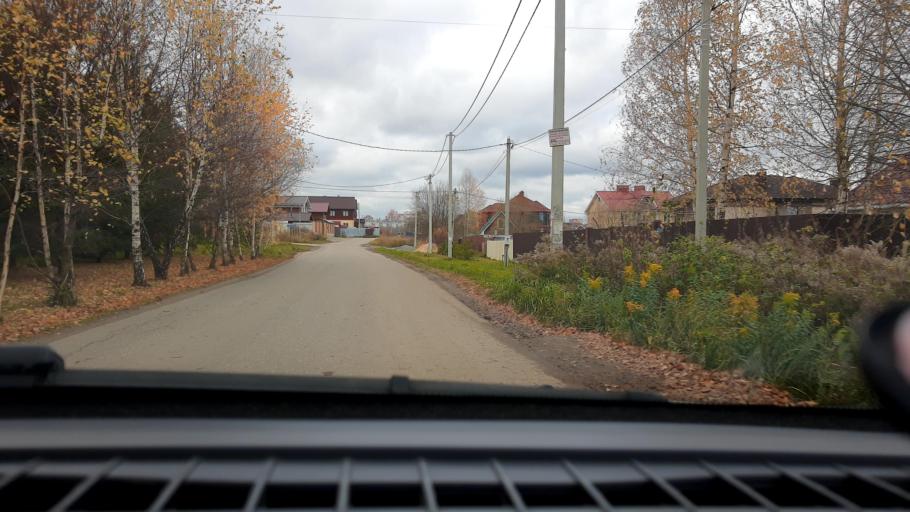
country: RU
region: Nizjnij Novgorod
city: Afonino
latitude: 56.2680
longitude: 44.0669
